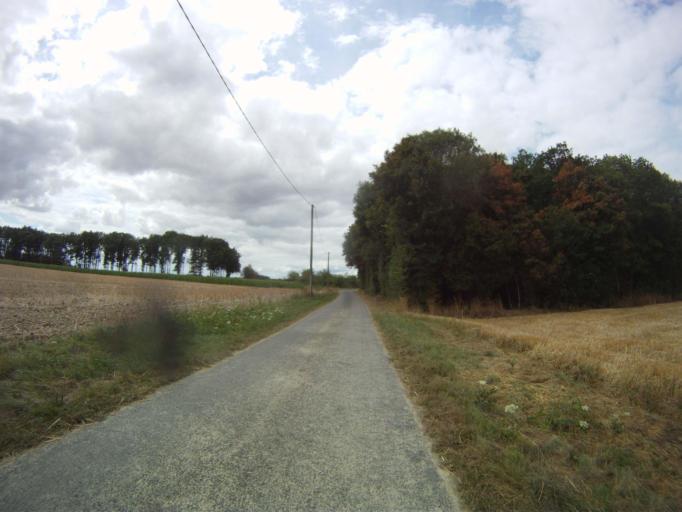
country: FR
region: Centre
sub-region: Departement du Loir-et-Cher
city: Montoire-sur-le-Loir
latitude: 47.6890
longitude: 0.8156
